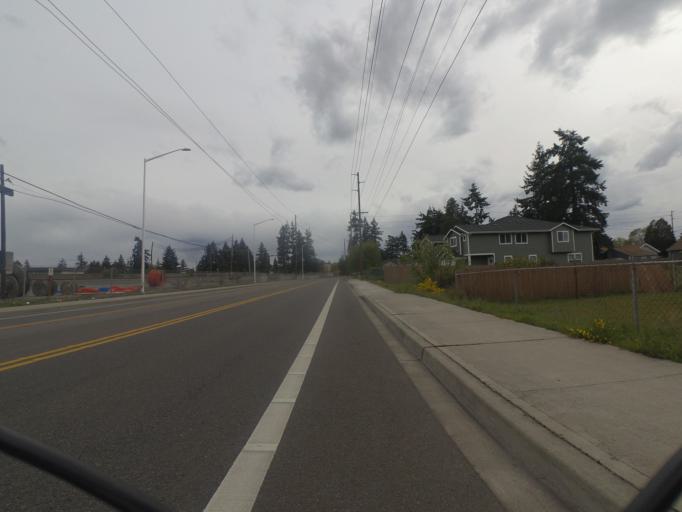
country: US
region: Washington
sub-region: Pierce County
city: McChord Air Force Base
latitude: 47.1573
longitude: -122.4955
